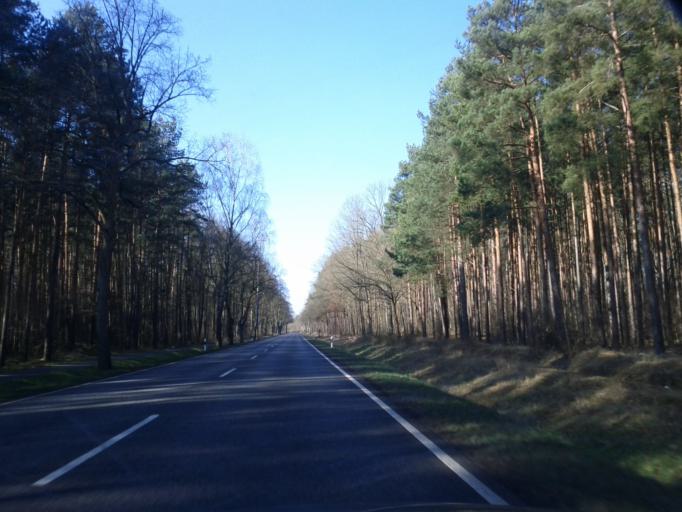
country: DE
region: Brandenburg
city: Spreenhagen
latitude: 52.4021
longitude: 13.9005
